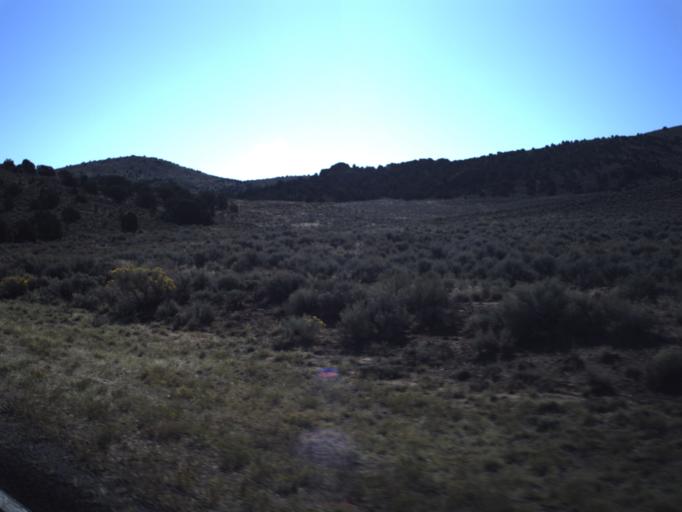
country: US
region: Utah
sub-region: Washington County
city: Enterprise
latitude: 37.6756
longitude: -113.5134
